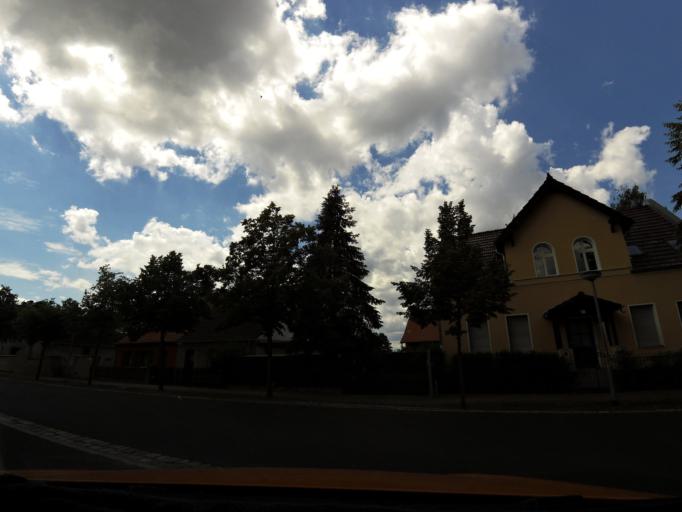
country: DE
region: Brandenburg
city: Munchehofe
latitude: 52.2586
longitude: 13.8000
